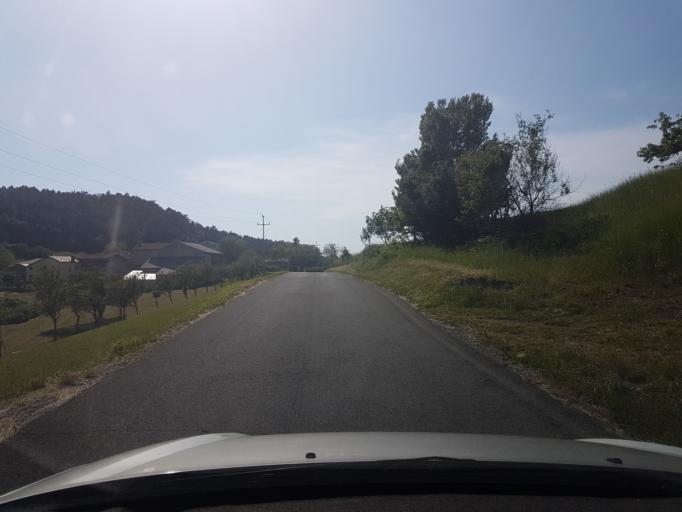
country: SI
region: Vipava
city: Vipava
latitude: 45.7697
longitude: 13.9644
